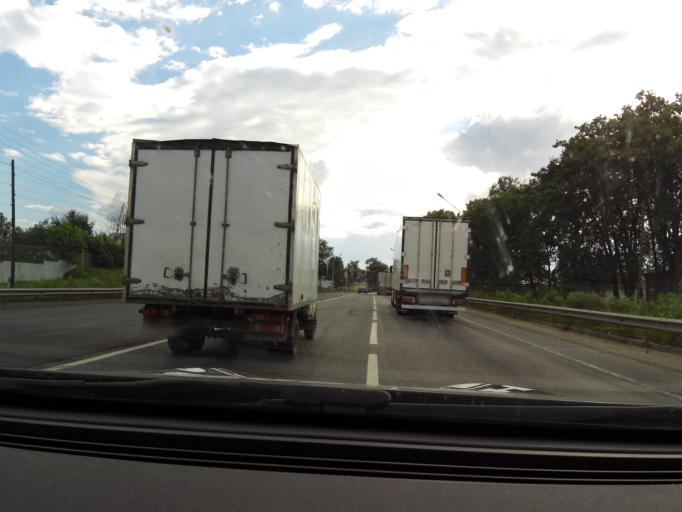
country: RU
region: Vladimir
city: Gorokhovets
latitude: 56.1976
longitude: 42.7003
